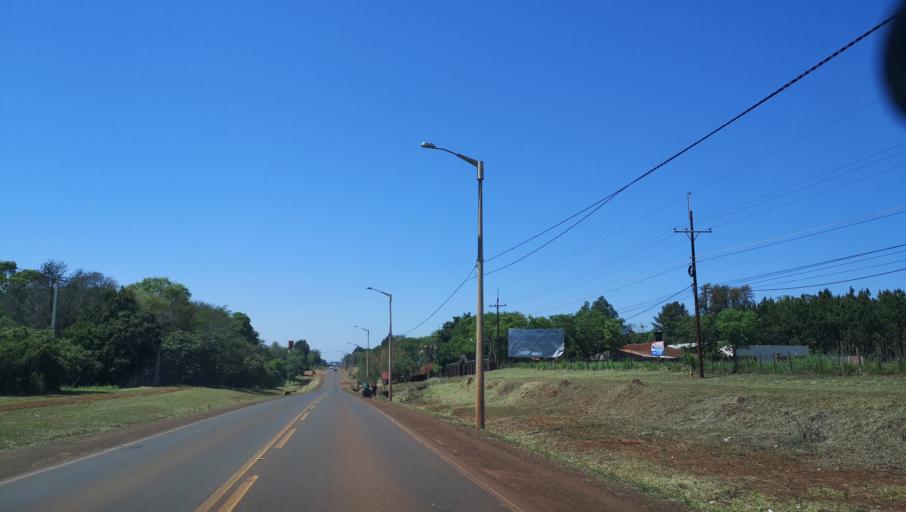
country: PY
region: Itapua
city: San Juan del Parana
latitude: -27.2752
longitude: -55.9507
